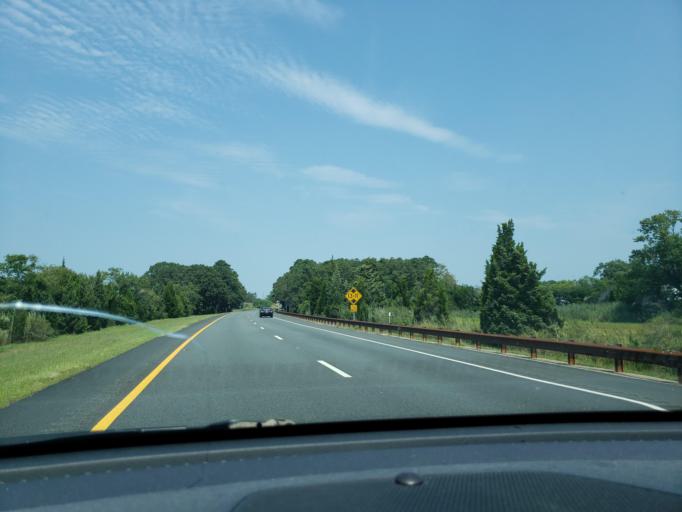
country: US
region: New Jersey
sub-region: Atlantic County
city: Somers Point
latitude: 39.3198
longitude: -74.6197
